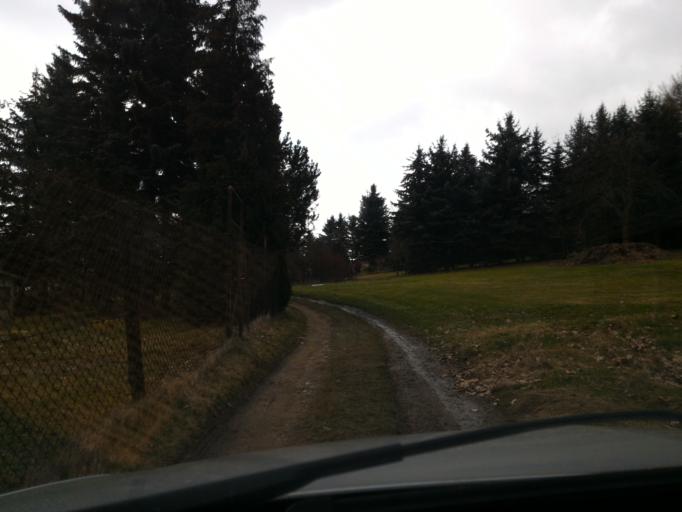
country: DE
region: Saxony
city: Grossschonau
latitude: 50.9038
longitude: 14.6663
